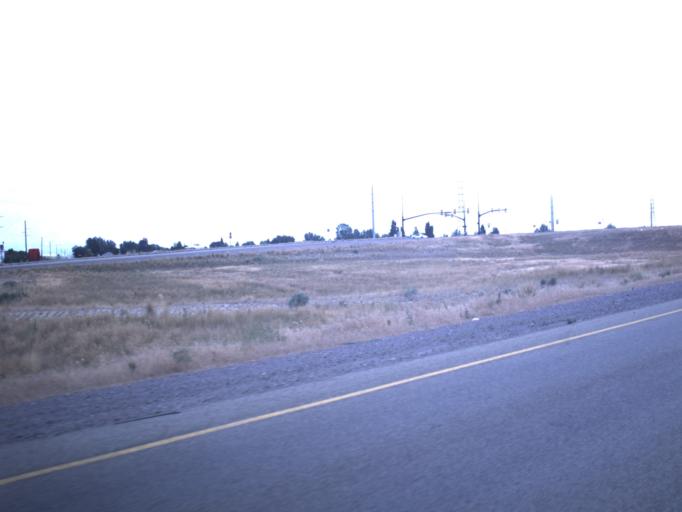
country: US
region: Utah
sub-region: Salt Lake County
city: Herriman
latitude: 40.5368
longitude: -112.0161
